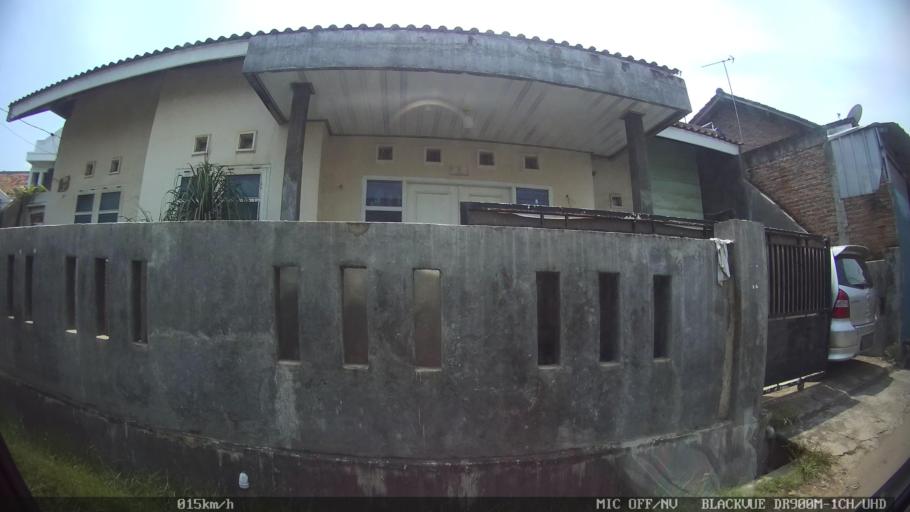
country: ID
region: Lampung
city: Bandarlampung
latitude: -5.4472
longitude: 105.2513
